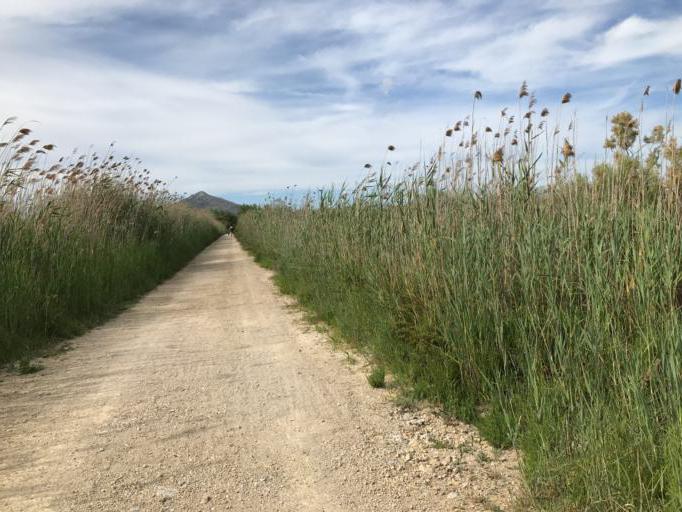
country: ES
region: Balearic Islands
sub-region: Illes Balears
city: Port d'Alcudia
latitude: 39.7965
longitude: 3.1115
